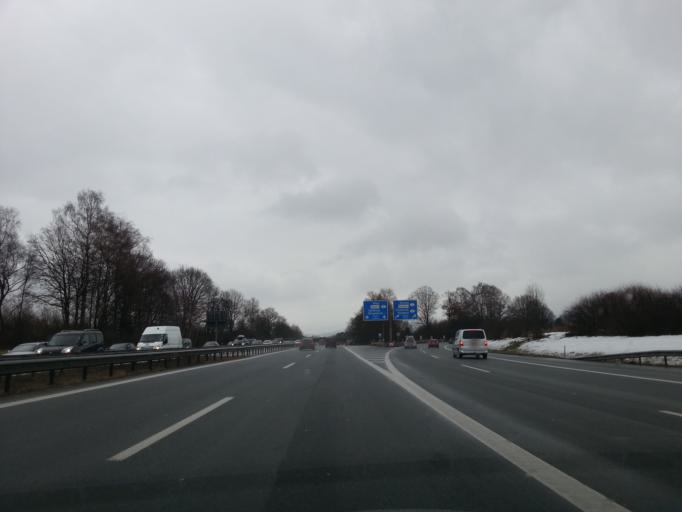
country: DE
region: Bavaria
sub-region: Upper Bavaria
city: Raubling
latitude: 47.8107
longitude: 12.0912
